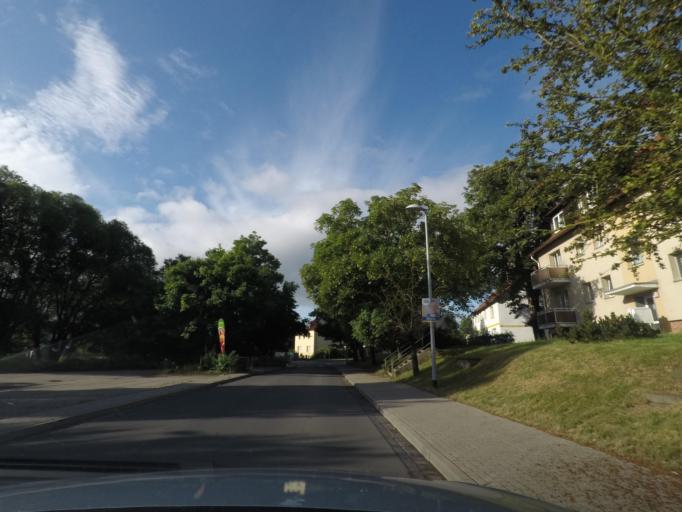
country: DE
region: Saxony-Anhalt
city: Derenburg
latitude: 51.8741
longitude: 10.9066
